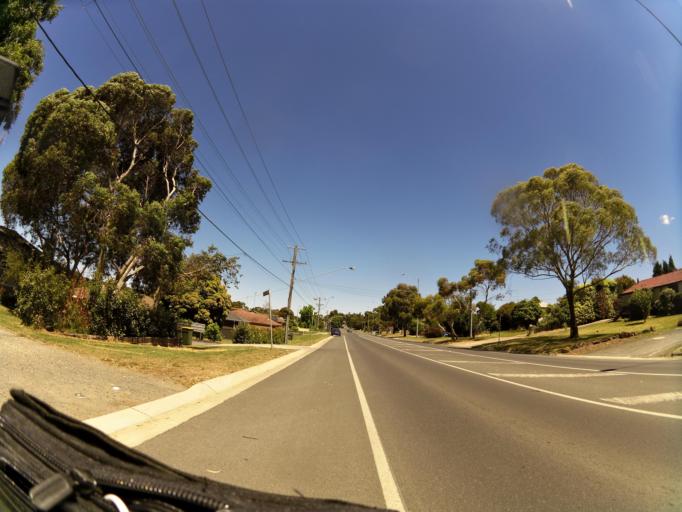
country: AU
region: Victoria
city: Mount Pleasant
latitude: -37.5914
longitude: 143.8671
